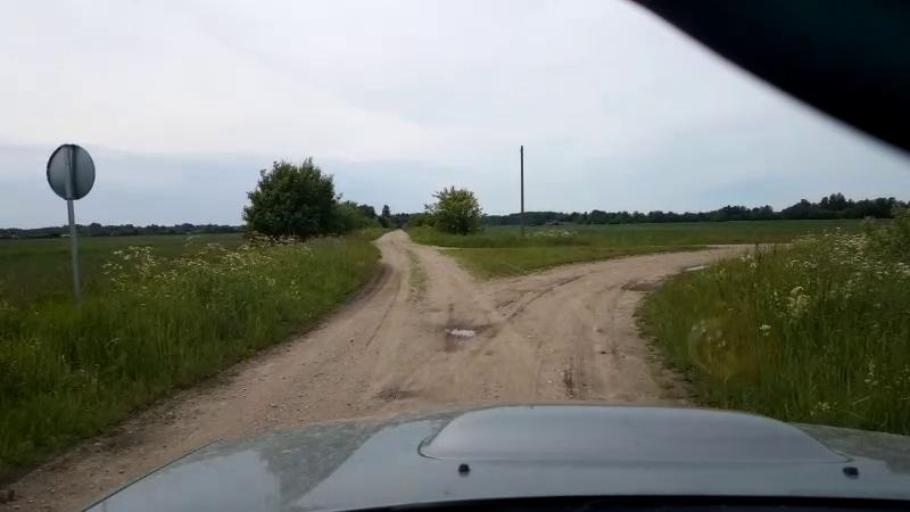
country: EE
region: Paernumaa
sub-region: Tootsi vald
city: Tootsi
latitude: 58.5353
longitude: 24.7361
